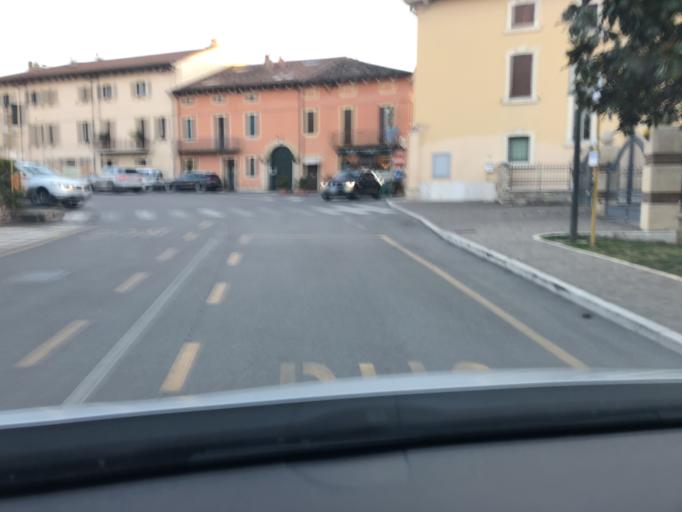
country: IT
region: Veneto
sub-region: Provincia di Verona
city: Sona
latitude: 45.4534
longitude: 10.8173
